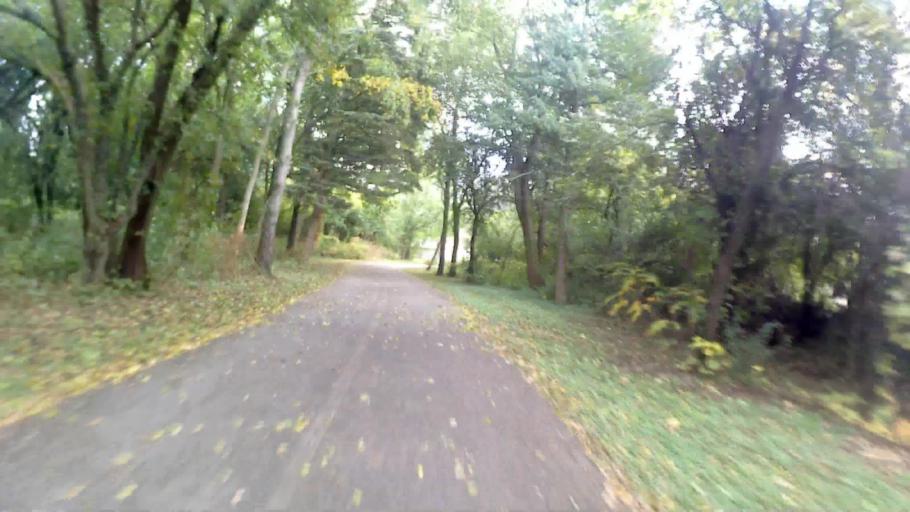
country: US
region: Illinois
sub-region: Kane County
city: Montgomery
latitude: 41.7456
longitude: -88.3466
